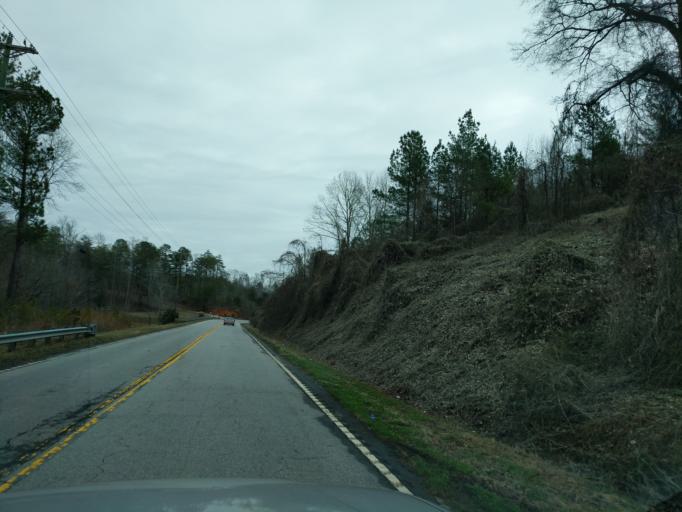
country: US
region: South Carolina
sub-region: Oconee County
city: Westminster
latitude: 34.6873
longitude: -83.1595
